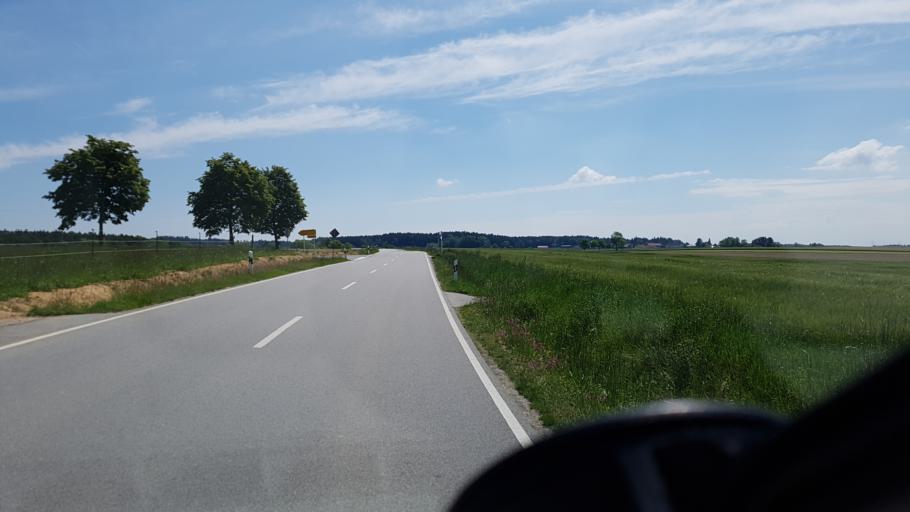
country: DE
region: Bavaria
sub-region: Lower Bavaria
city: Triftern
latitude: 48.3902
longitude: 13.0381
